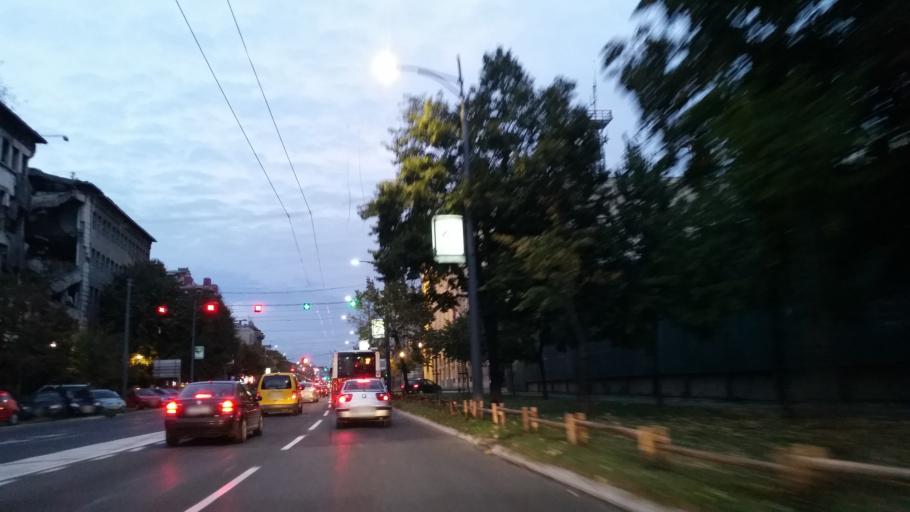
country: RS
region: Central Serbia
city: Belgrade
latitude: 44.7994
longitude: 20.4527
